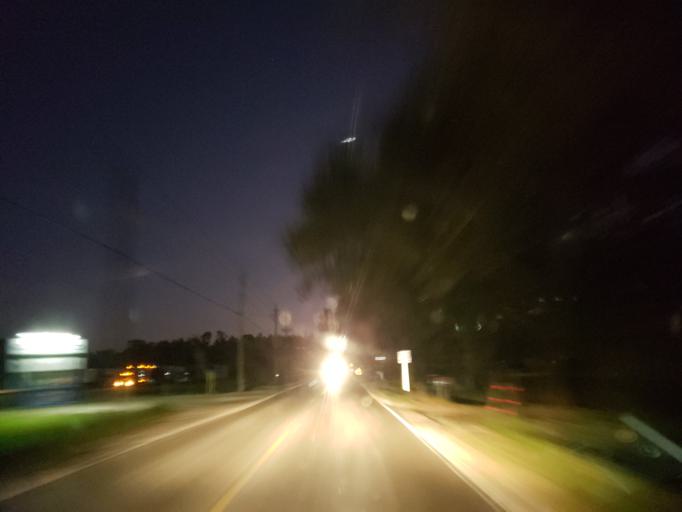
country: US
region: Florida
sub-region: Hillsborough County
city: Dover
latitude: 27.9704
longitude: -82.2197
